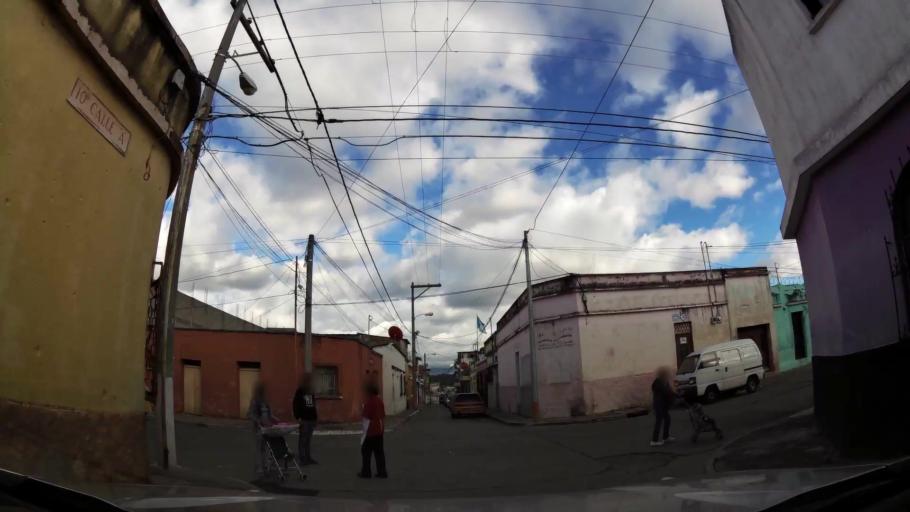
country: GT
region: Guatemala
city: Guatemala City
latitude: 14.6368
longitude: -90.5017
